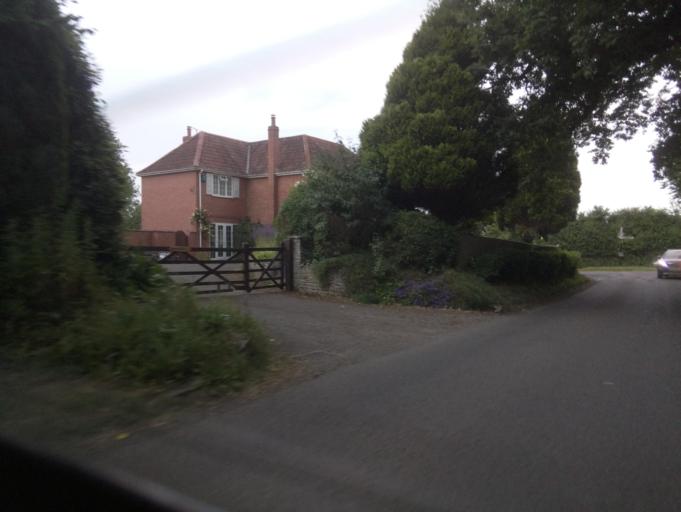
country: GB
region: England
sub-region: Somerset
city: Yeovil
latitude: 50.9232
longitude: -2.5868
